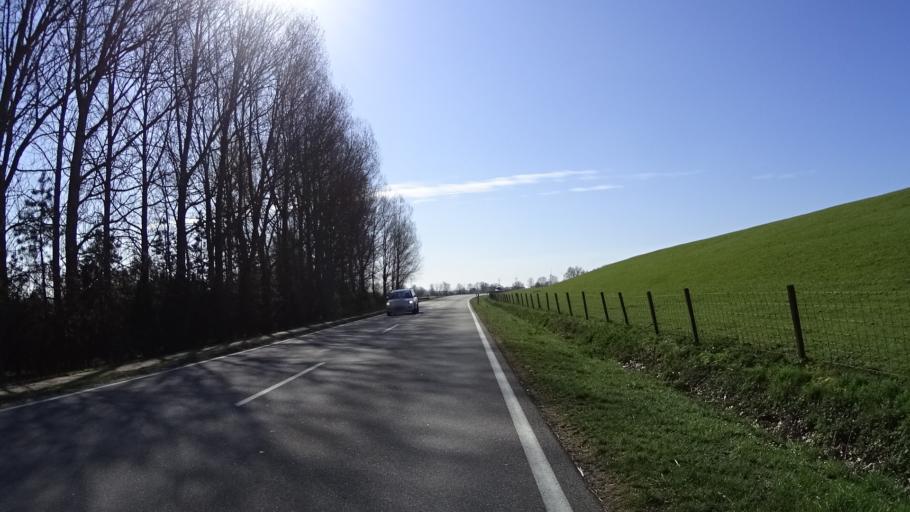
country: DE
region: Lower Saxony
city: Jemgum
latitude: 53.2893
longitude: 7.4034
